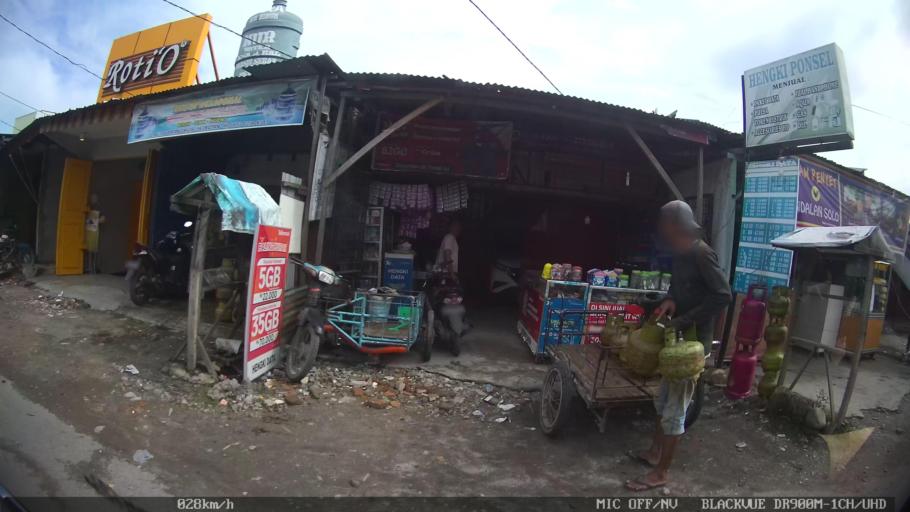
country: ID
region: North Sumatra
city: Medan
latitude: 3.6207
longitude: 98.7286
